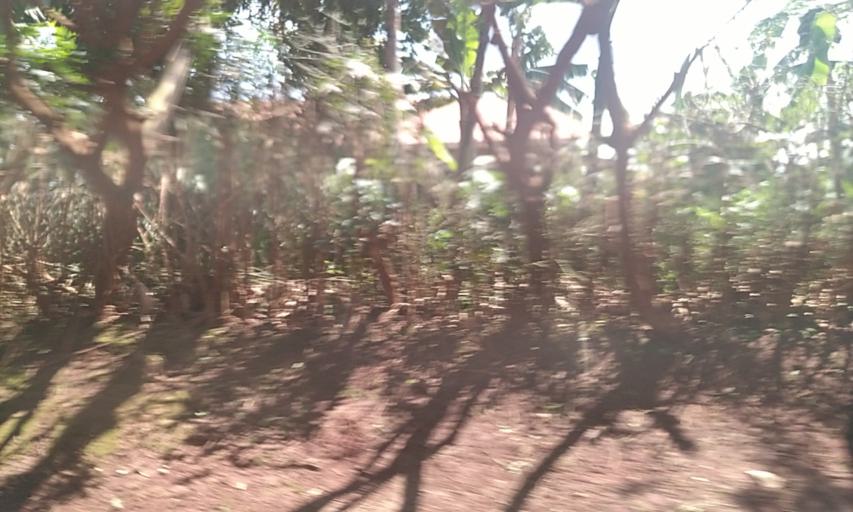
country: UG
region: Central Region
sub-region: Wakiso District
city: Wakiso
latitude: 0.4094
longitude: 32.4733
